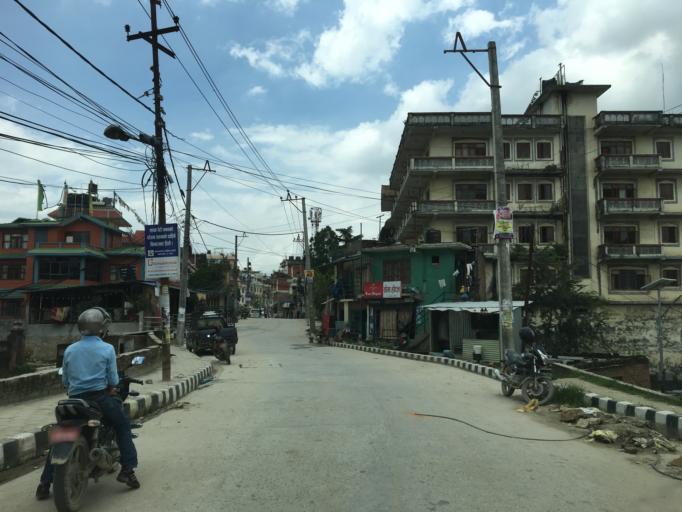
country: NP
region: Central Region
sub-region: Bagmati Zone
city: Kathmandu
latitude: 27.7271
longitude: 85.3647
